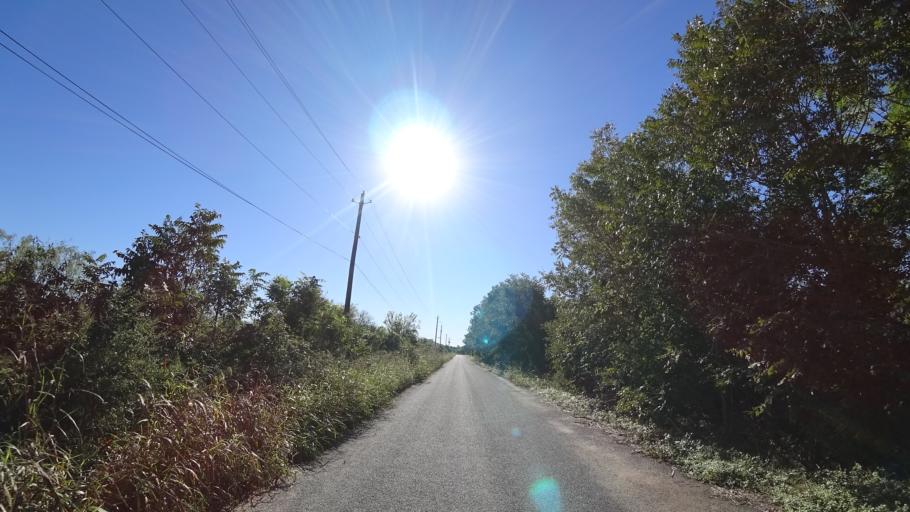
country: US
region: Texas
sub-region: Travis County
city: Hornsby Bend
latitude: 30.2387
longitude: -97.6557
